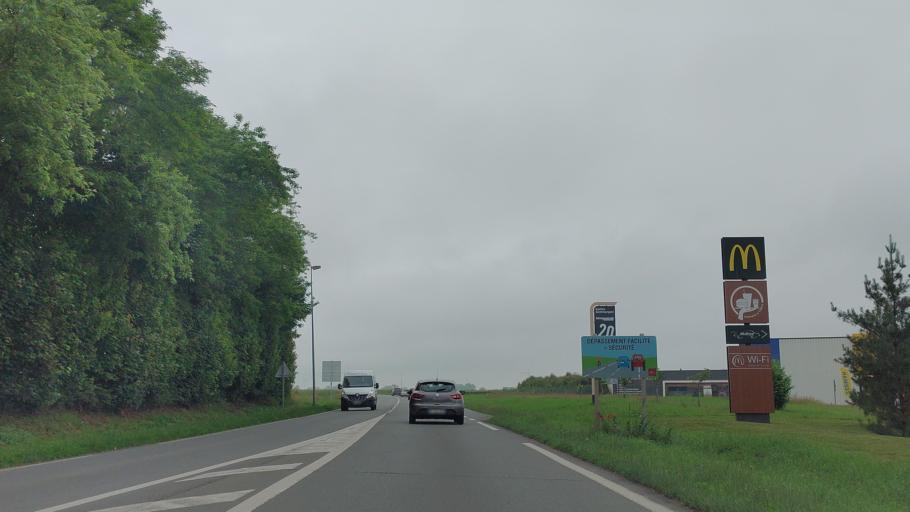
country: FR
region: Picardie
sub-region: Departement de la Somme
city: Woincourt
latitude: 50.0737
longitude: 1.5358
